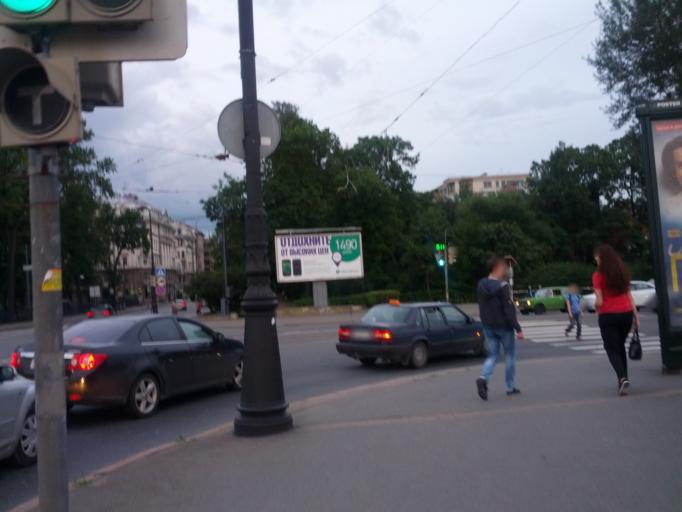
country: RU
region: Leningrad
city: Chernaya Rechka
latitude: 59.9768
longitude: 30.3019
